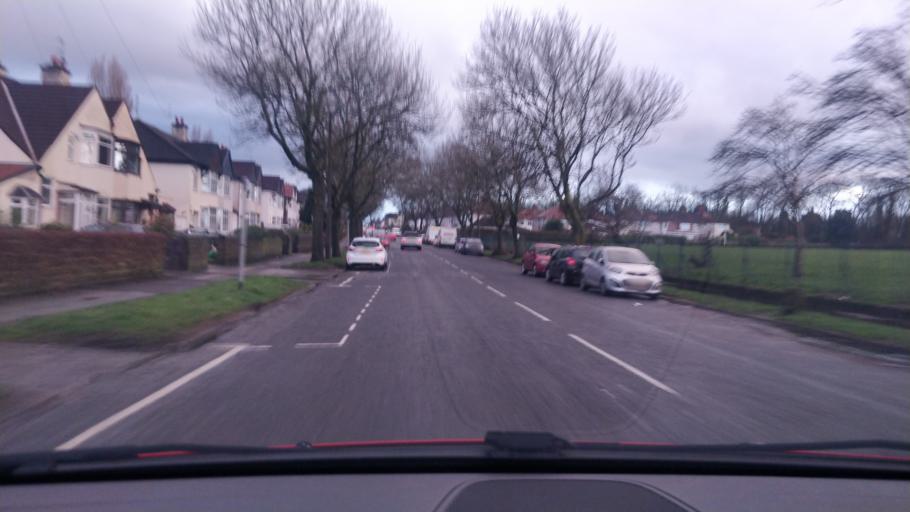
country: GB
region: England
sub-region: Knowsley
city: Huyton
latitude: 53.4139
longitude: -2.8921
